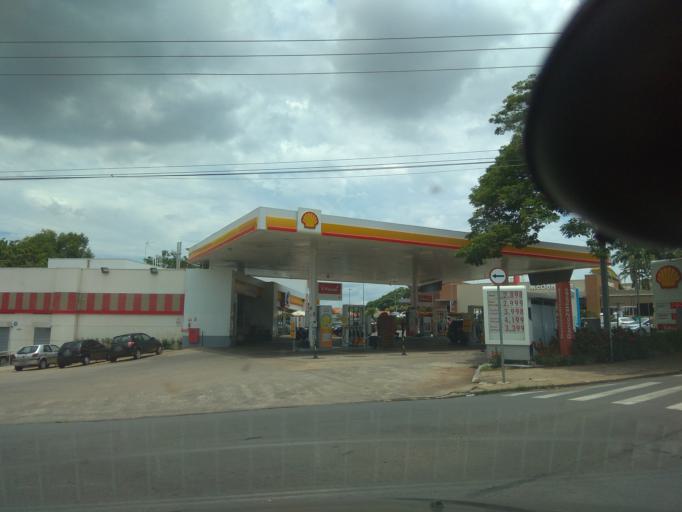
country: BR
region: Sao Paulo
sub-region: Campinas
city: Campinas
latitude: -22.8251
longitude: -47.0798
